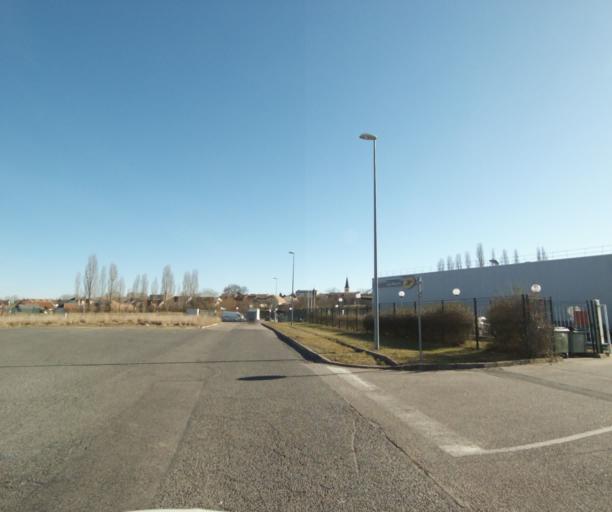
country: FR
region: Lorraine
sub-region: Departement de Meurthe-et-Moselle
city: Vandoeuvre-les-Nancy
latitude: 48.6559
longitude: 6.1922
